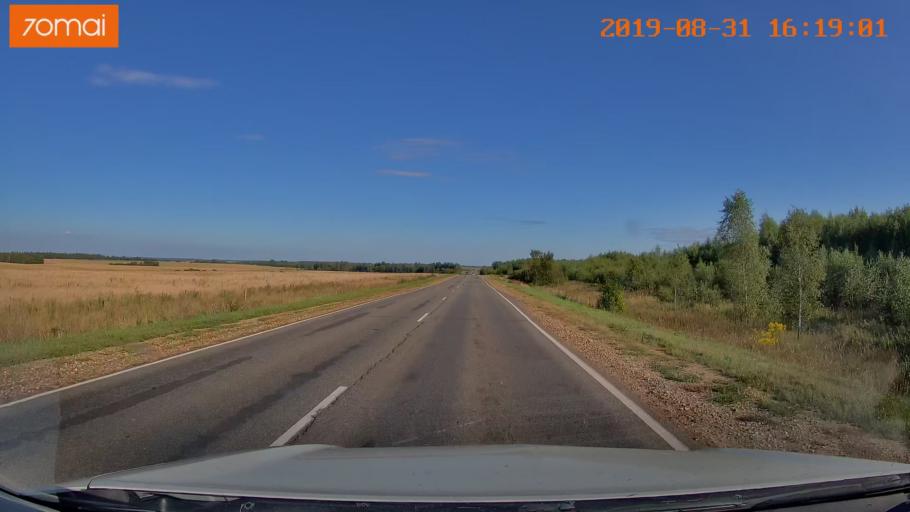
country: RU
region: Kaluga
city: Nikola-Lenivets
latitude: 54.5321
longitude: 35.5683
